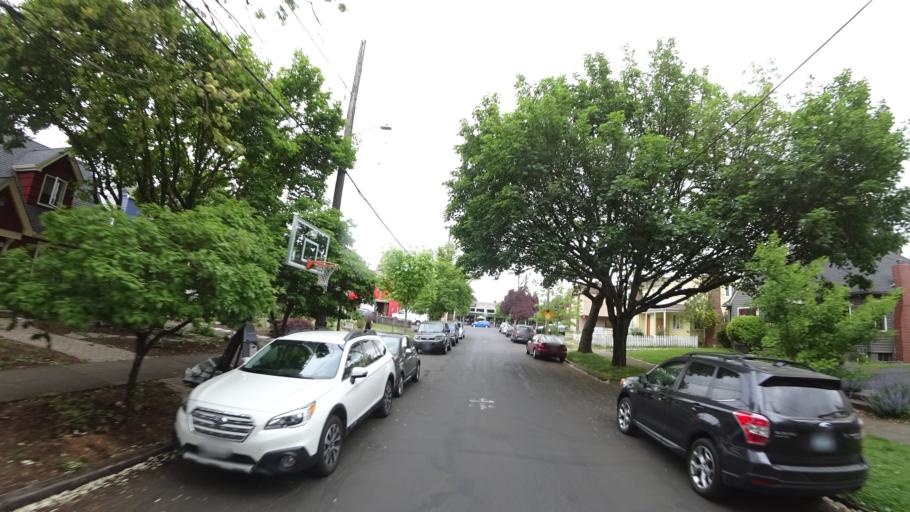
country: US
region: Oregon
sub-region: Multnomah County
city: Portland
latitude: 45.5476
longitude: -122.6188
